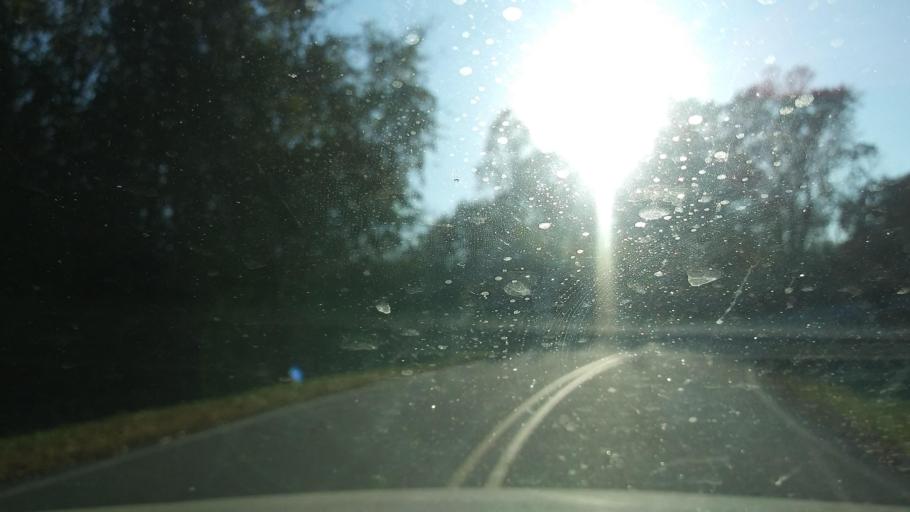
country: US
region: North Carolina
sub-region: Guilford County
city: Pleasant Garden
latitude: 36.0012
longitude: -79.7614
